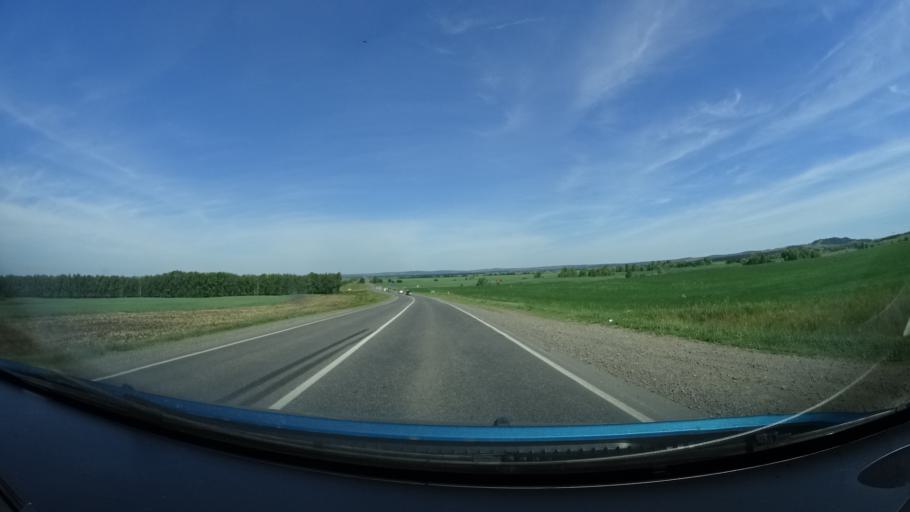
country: RU
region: Bashkortostan
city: Blagoveshchensk
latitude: 55.1827
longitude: 55.8515
